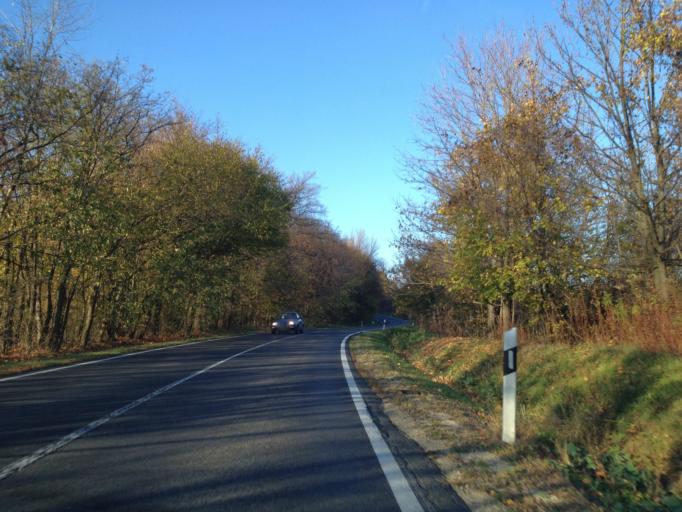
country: HU
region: Veszprem
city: Zirc
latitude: 47.3172
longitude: 17.8766
